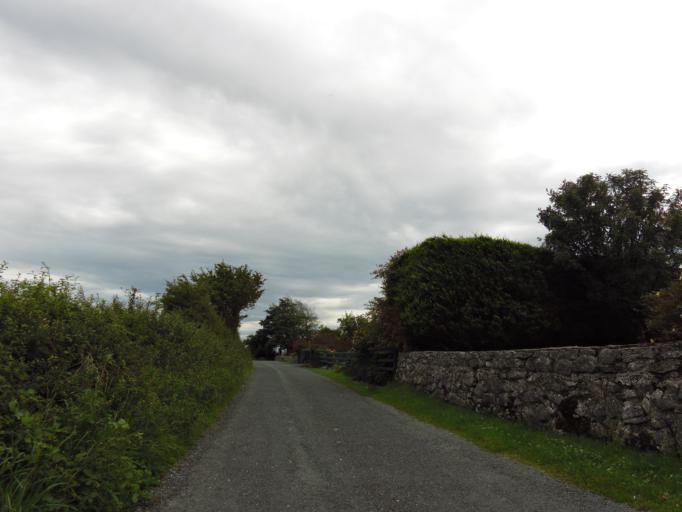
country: IE
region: Connaught
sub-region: County Galway
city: Gaillimh
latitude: 53.3172
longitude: -9.0489
